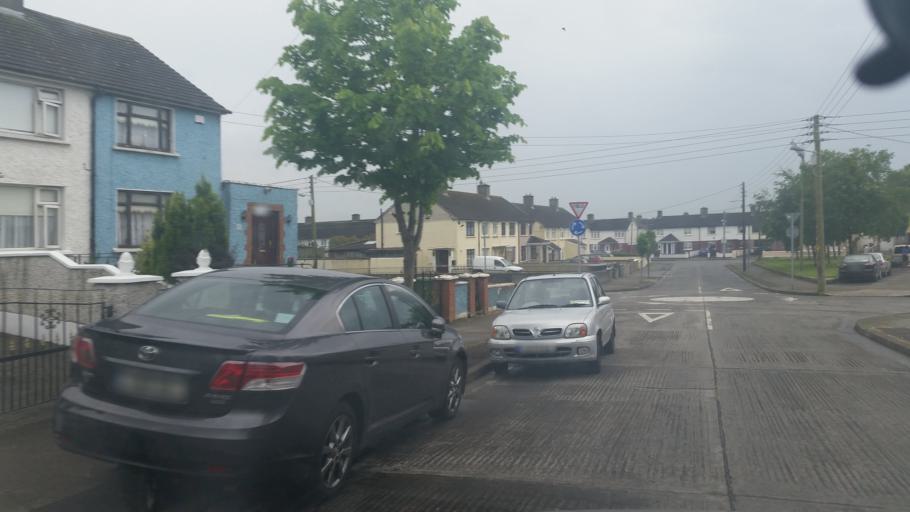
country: IE
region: Leinster
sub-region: Dublin City
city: Finglas
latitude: 53.3878
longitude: -6.3156
